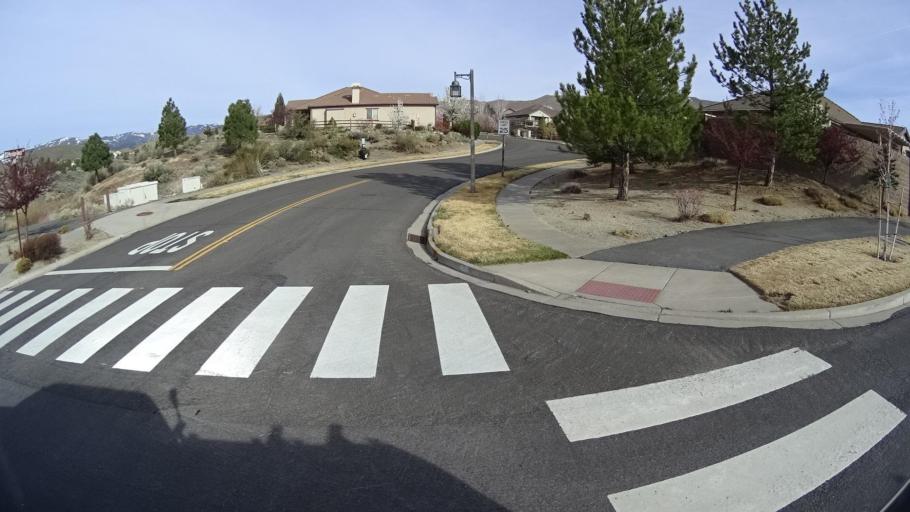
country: US
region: Nevada
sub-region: Washoe County
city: Mogul
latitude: 39.5222
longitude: -119.9475
